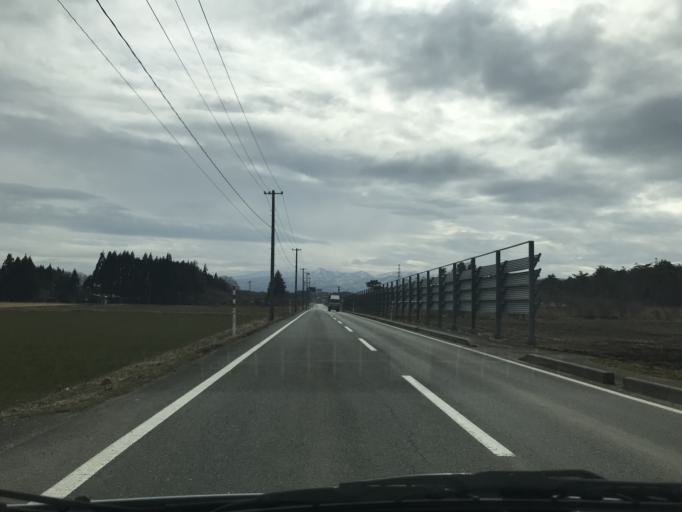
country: JP
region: Iwate
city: Hanamaki
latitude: 39.3708
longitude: 141.0027
